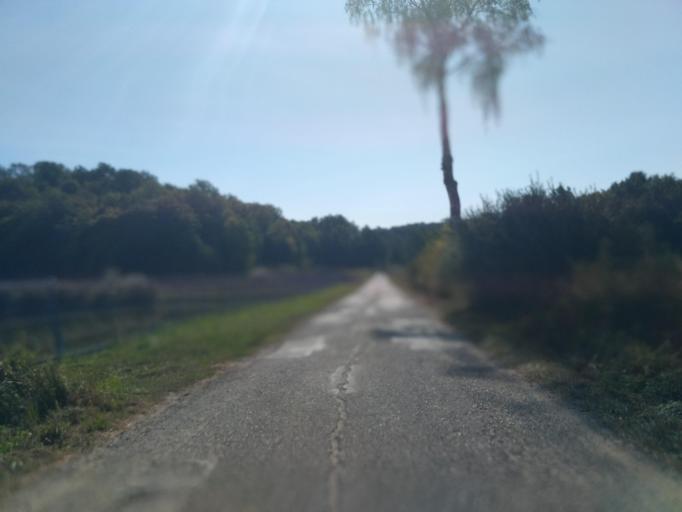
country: PL
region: Subcarpathian Voivodeship
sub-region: Powiat brzozowski
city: Brzozow
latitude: 49.7127
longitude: 22.0388
